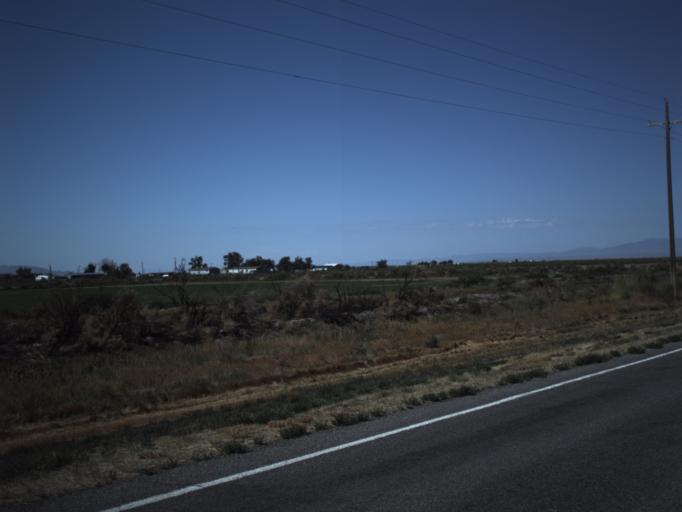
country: US
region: Utah
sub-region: Millard County
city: Delta
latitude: 39.3308
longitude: -112.6762
